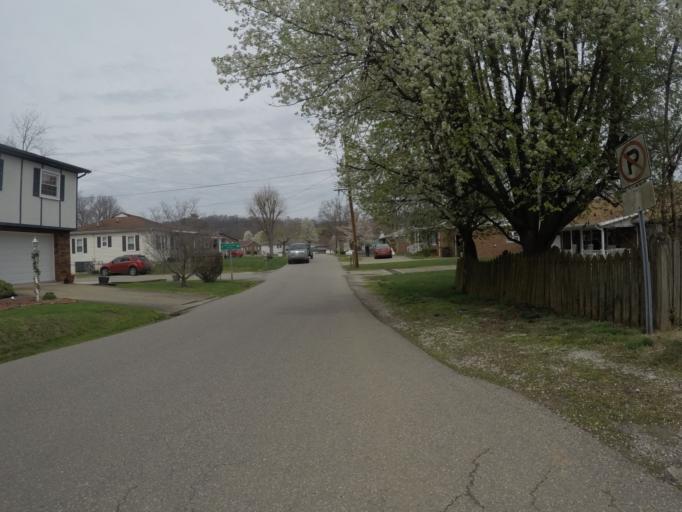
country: US
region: West Virginia
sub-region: Cabell County
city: Barboursville
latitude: 38.4211
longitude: -82.3046
